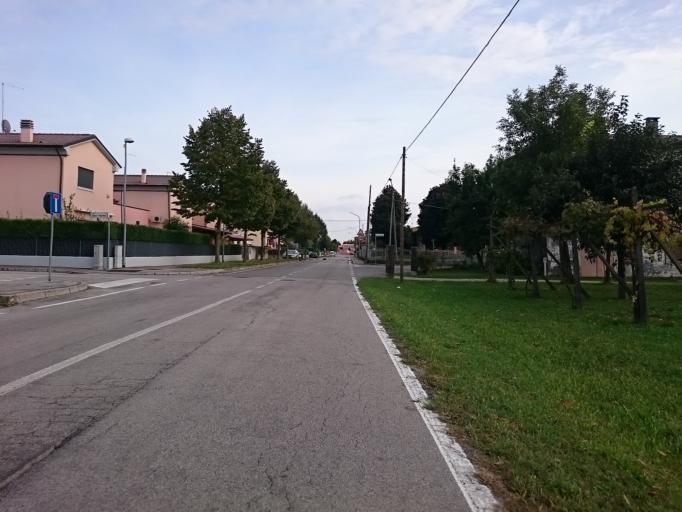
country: IT
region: Veneto
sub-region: Provincia di Vicenza
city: Grumolo delle Abbadesse
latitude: 45.5412
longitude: 11.6853
